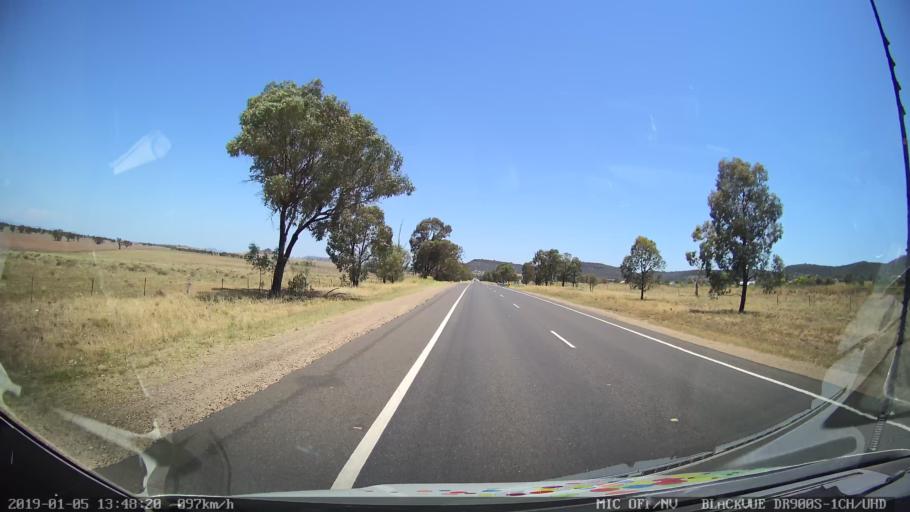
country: AU
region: New South Wales
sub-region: Gunnedah
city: Gunnedah
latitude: -31.0004
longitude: 150.2786
